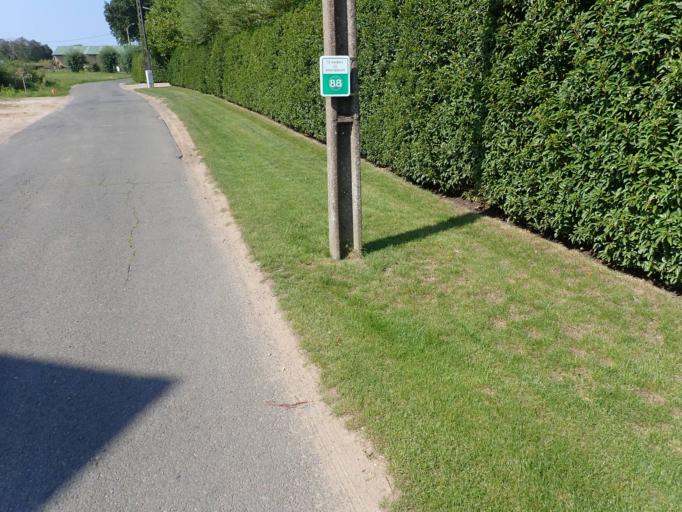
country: BE
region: Flanders
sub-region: Provincie Antwerpen
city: Sint-Amands
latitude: 51.0318
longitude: 4.2520
